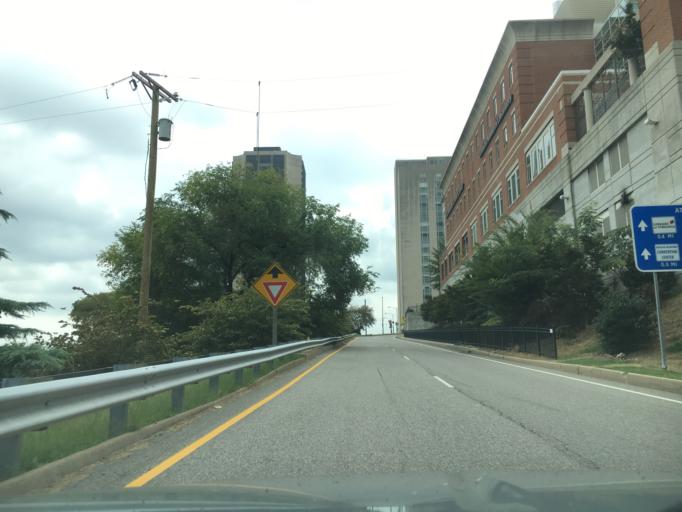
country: US
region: Virginia
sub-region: City of Richmond
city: Richmond
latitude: 37.5392
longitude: -77.4282
